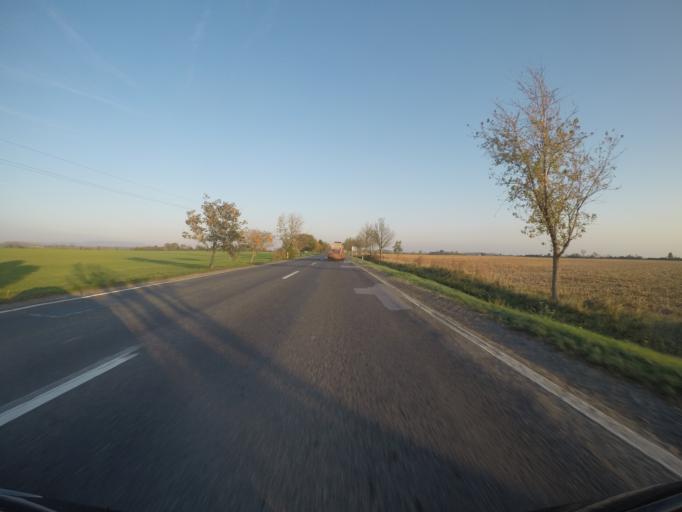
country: HU
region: Baranya
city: Szentlorinc
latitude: 46.0424
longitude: 17.9198
